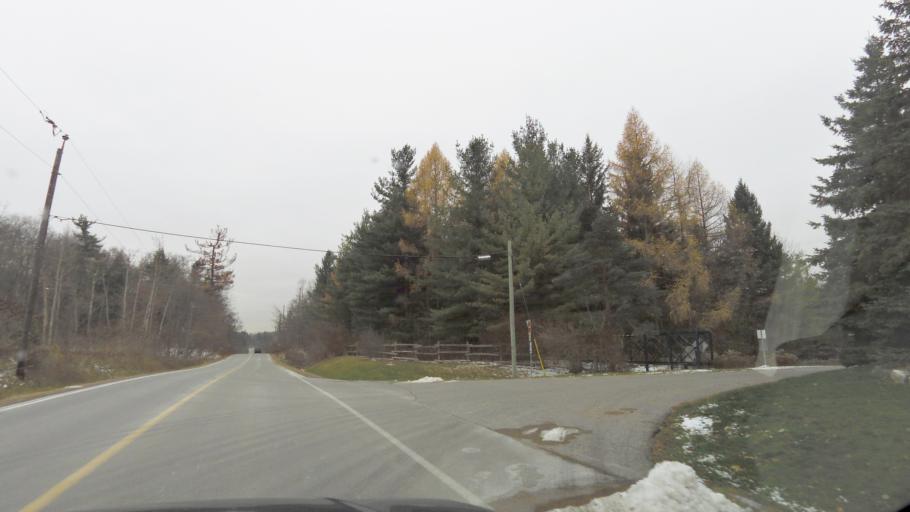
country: CA
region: Ontario
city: Vaughan
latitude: 43.8295
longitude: -79.5841
